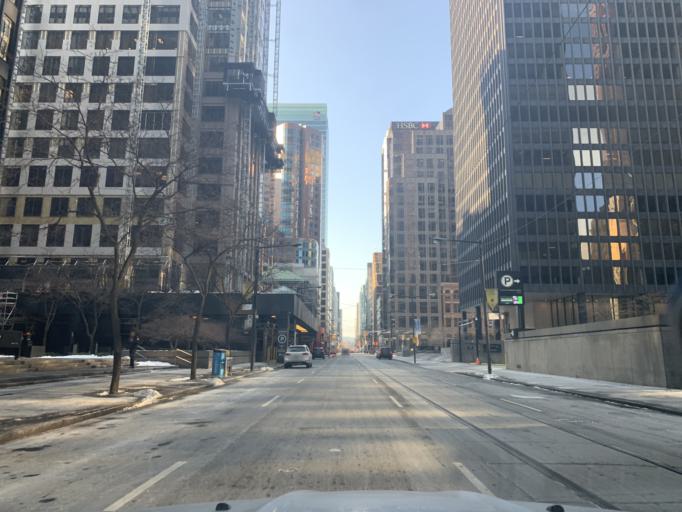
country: CA
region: Ontario
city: Toronto
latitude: 43.6469
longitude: -79.3812
